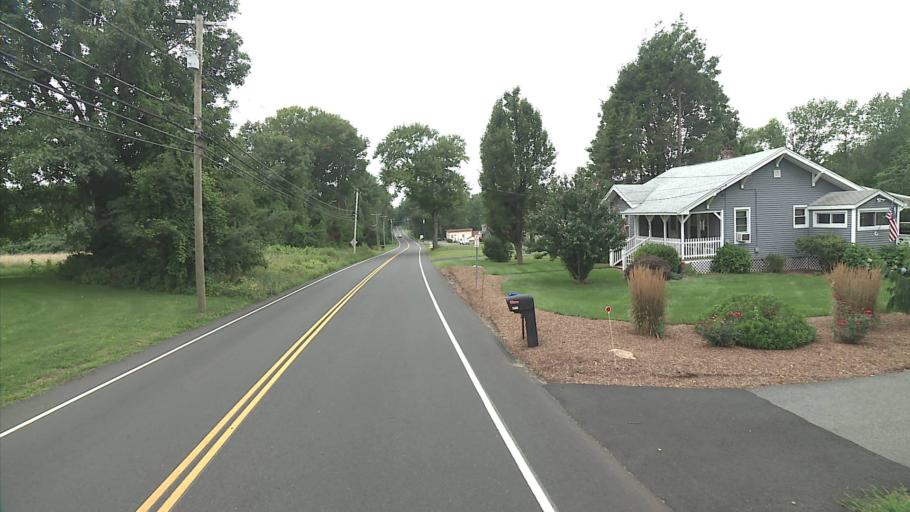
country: US
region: Connecticut
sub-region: Tolland County
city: Rockville
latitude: 41.8699
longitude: -72.4142
